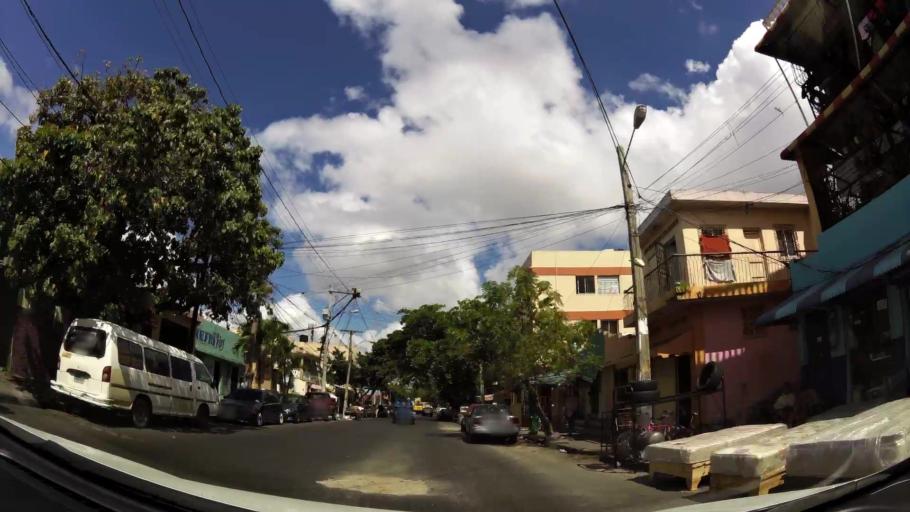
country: DO
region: Nacional
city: Ensanche Luperon
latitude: 18.4970
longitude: -69.8909
